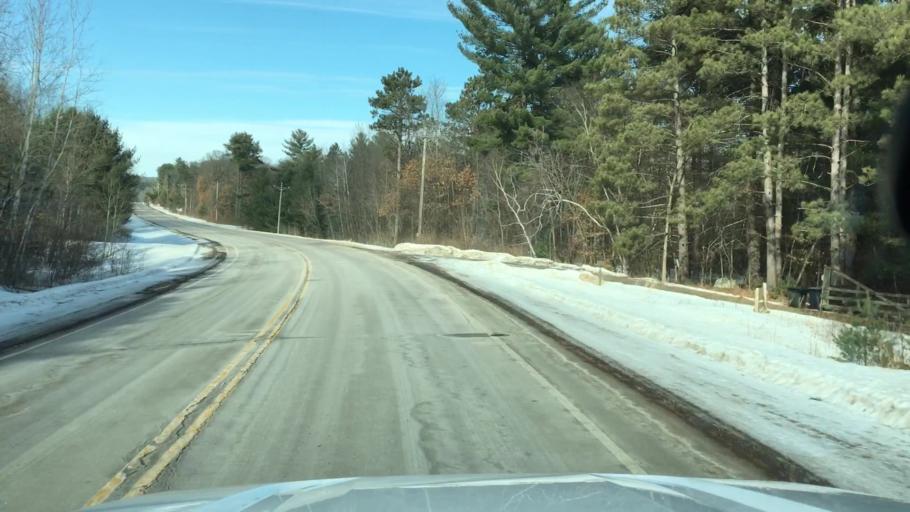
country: US
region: Wisconsin
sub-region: Polk County
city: Saint Croix Falls
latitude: 45.4582
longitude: -92.6746
